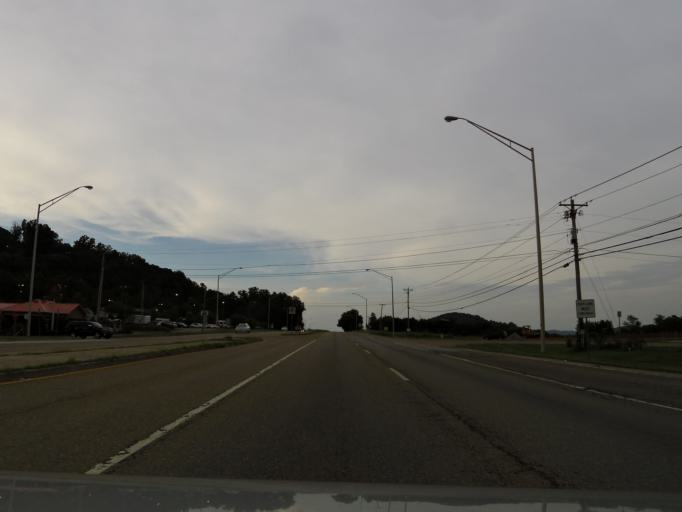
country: US
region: Tennessee
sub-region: Blount County
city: Alcoa
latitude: 35.8402
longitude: -83.9688
